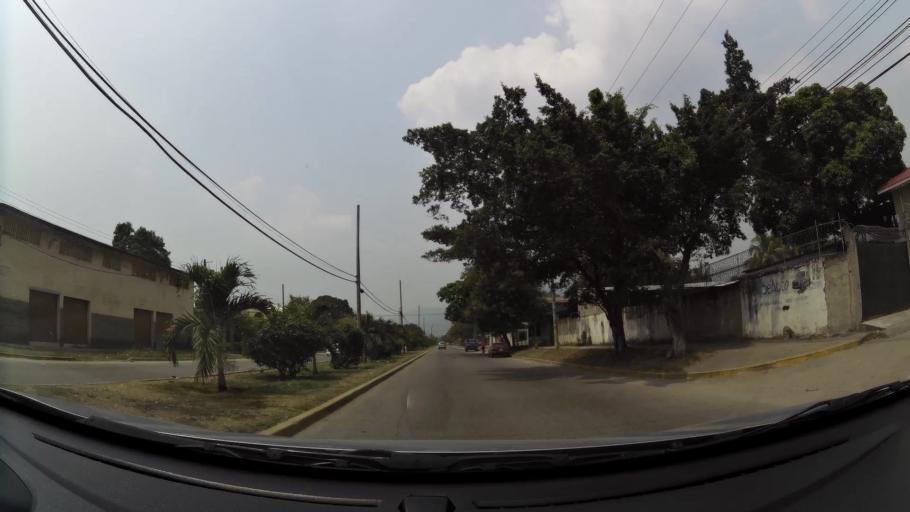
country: HN
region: Cortes
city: San Pedro Sula
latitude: 15.4859
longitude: -88.0203
